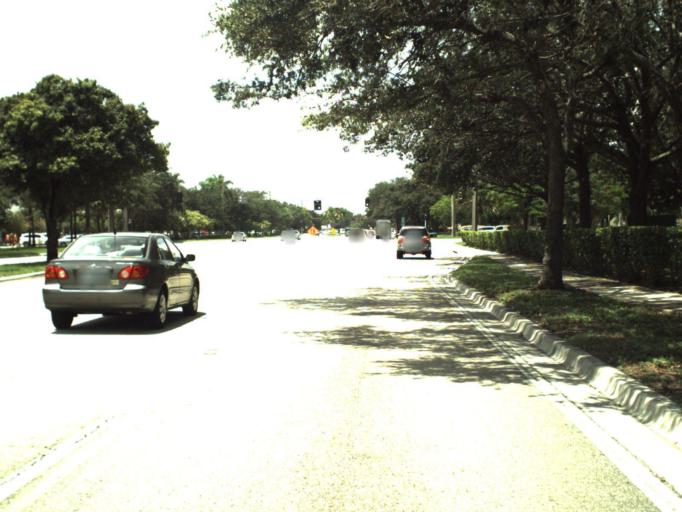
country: US
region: Florida
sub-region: Broward County
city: Tamarac
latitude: 26.2395
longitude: -80.2504
